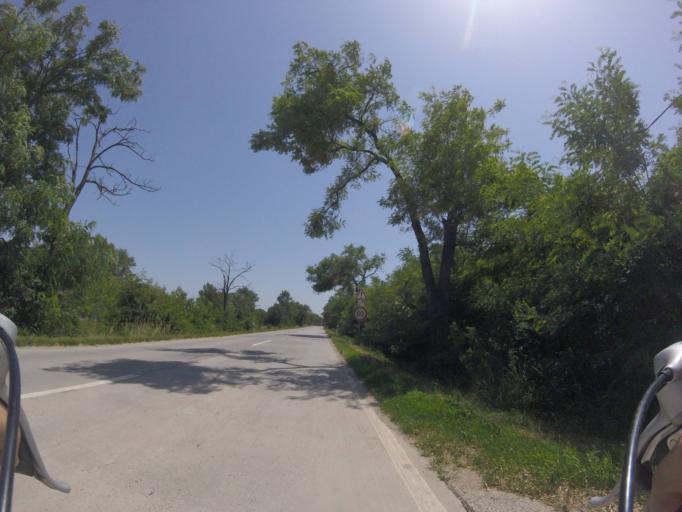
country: HU
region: Pest
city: Dunavarsany
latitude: 47.2565
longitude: 19.0526
